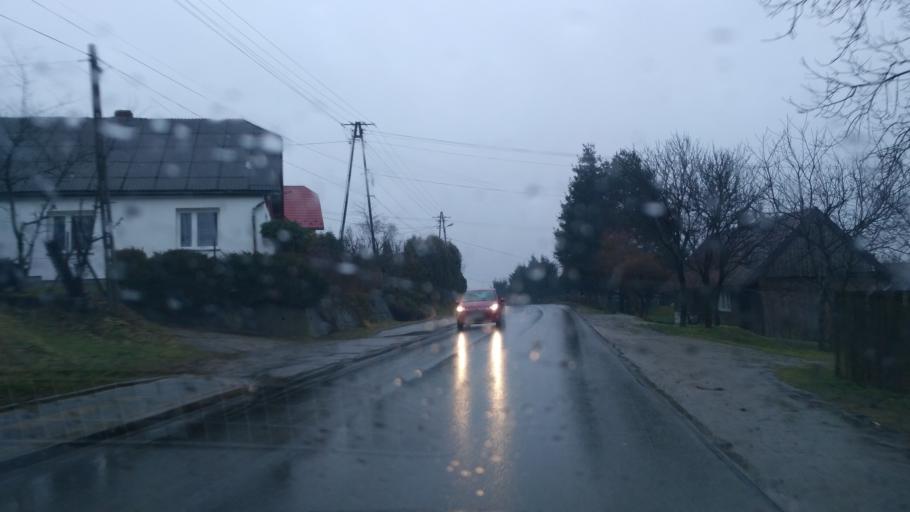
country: PL
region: Subcarpathian Voivodeship
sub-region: Powiat krosnienski
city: Kroscienko Wyzne
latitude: 49.6801
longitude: 21.8252
